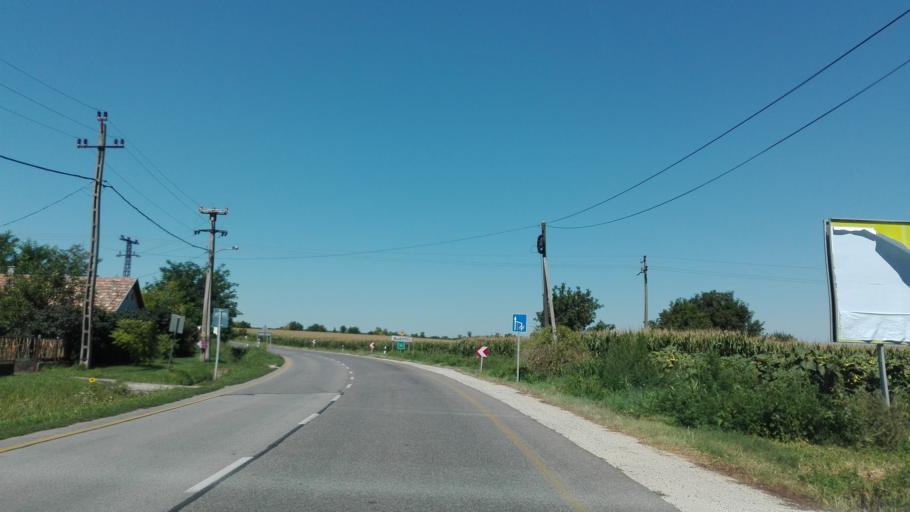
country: HU
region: Fejer
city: Mezoszilas
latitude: 46.8306
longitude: 18.4692
